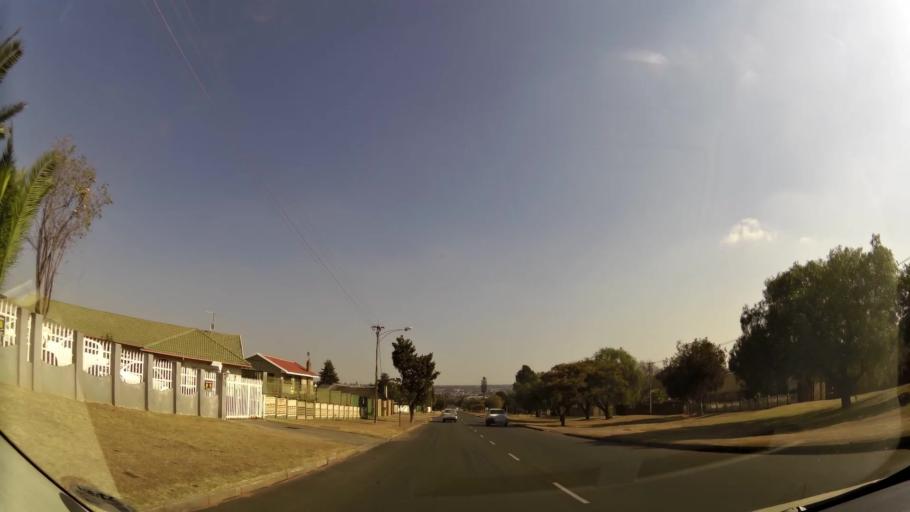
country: ZA
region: Gauteng
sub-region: West Rand District Municipality
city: Randfontein
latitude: -26.1575
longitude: 27.6960
